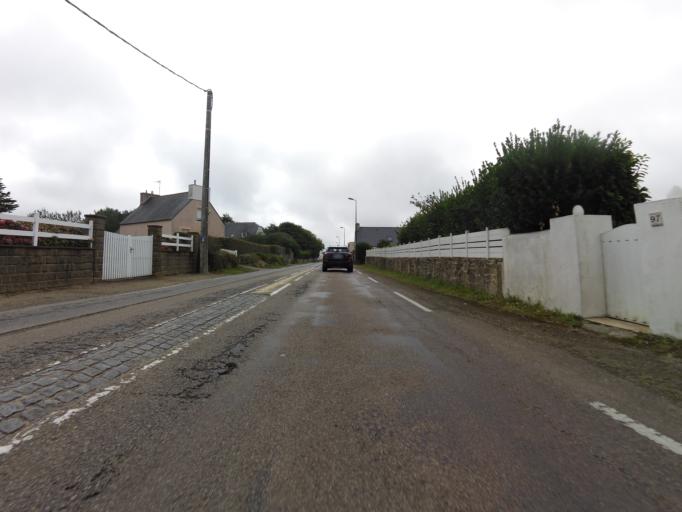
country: FR
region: Brittany
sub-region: Departement du Finistere
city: Plozevet
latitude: 47.9925
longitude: -4.4354
